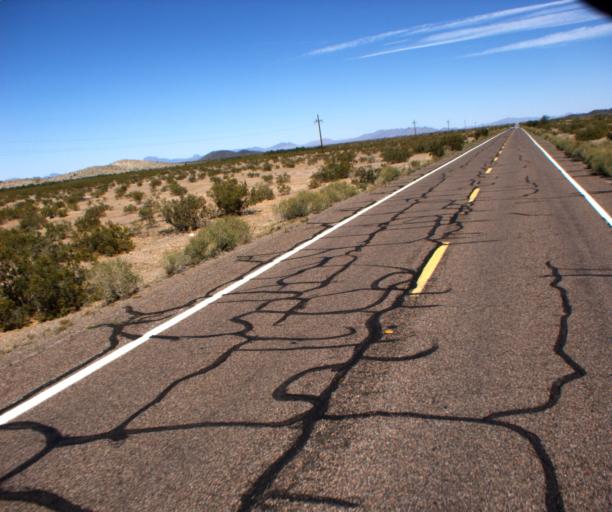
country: US
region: Arizona
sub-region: Maricopa County
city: Gila Bend
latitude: 32.7709
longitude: -112.8158
